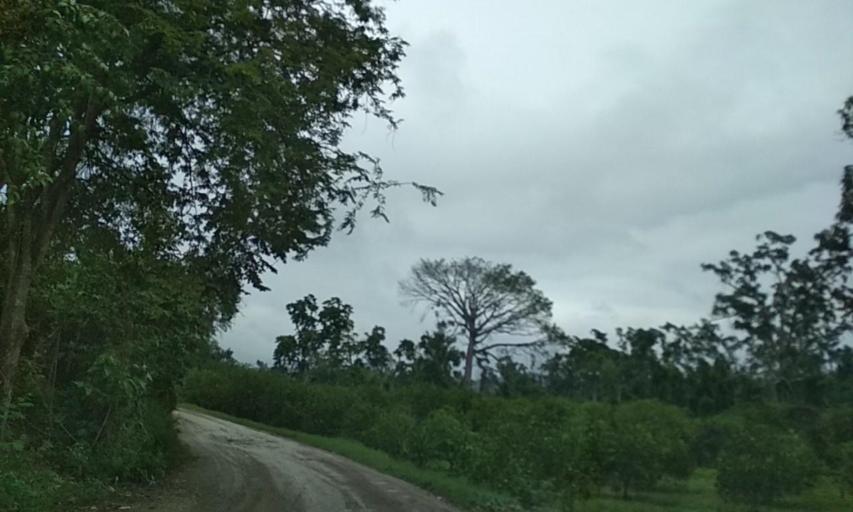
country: MX
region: Veracruz
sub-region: Papantla
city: El Chote
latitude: 20.3841
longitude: -97.3528
